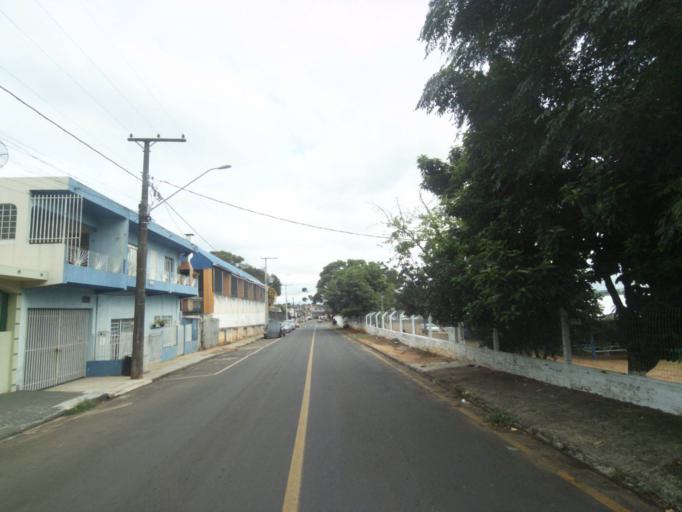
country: BR
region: Parana
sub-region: Telemaco Borba
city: Telemaco Borba
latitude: -24.3311
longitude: -50.6274
